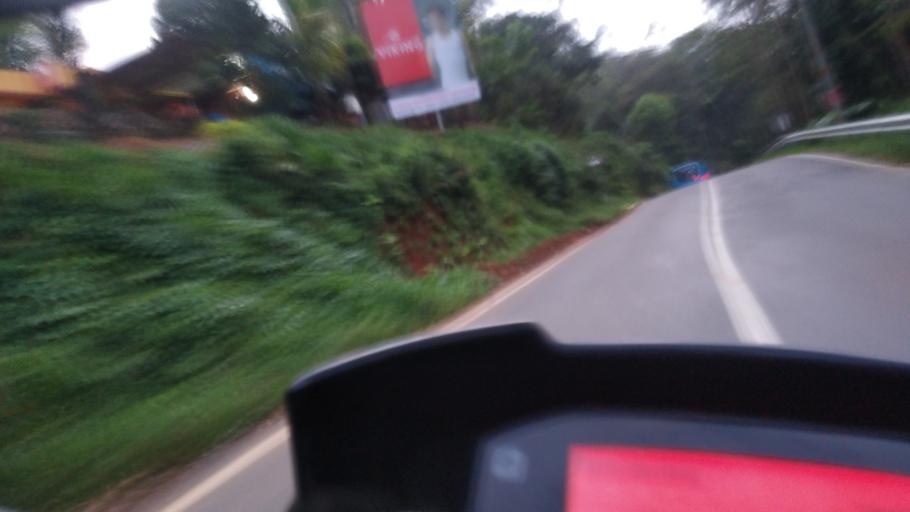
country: IN
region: Kerala
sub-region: Idukki
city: Munnar
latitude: 9.9688
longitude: 77.1259
